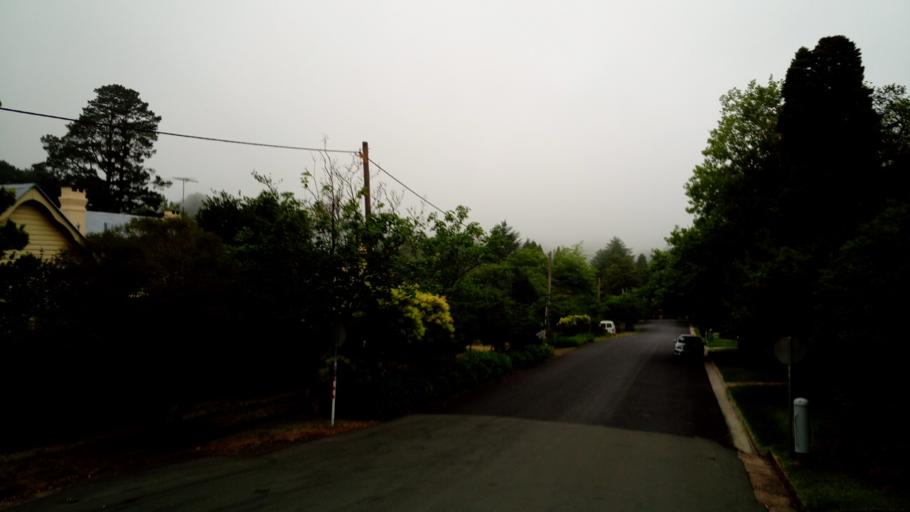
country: AU
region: New South Wales
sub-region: Blue Mountains Municipality
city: Leura
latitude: -33.7191
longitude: 150.3289
